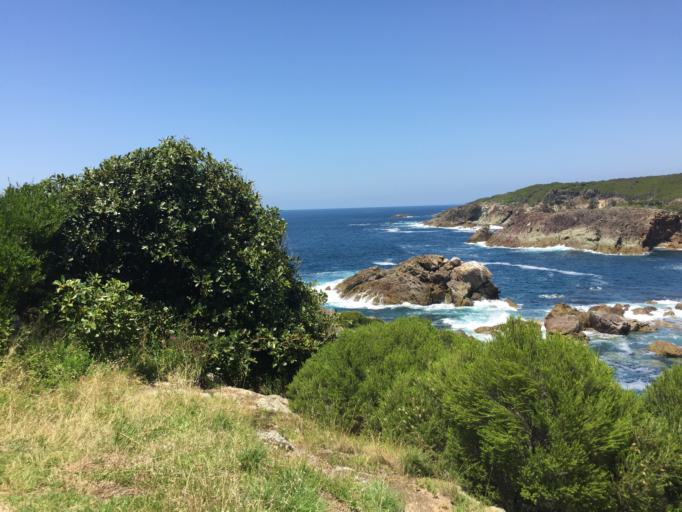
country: AU
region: New South Wales
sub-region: Bega Valley
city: Bega
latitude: -36.7372
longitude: 149.9845
